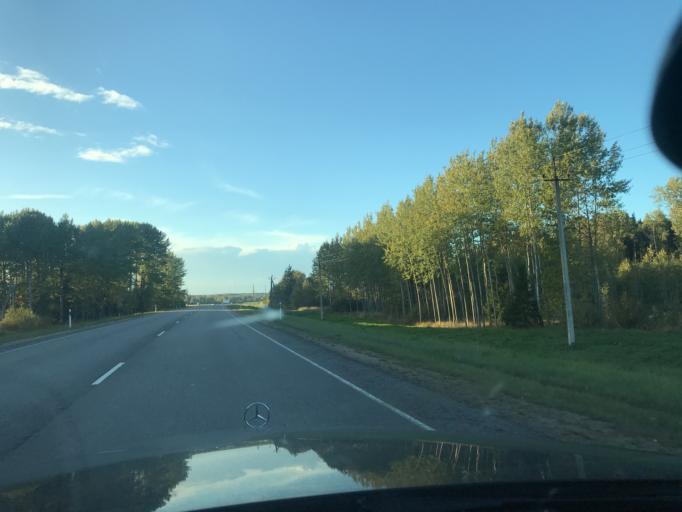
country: EE
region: Vorumaa
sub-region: Voru linn
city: Voru
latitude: 57.8521
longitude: 27.0302
